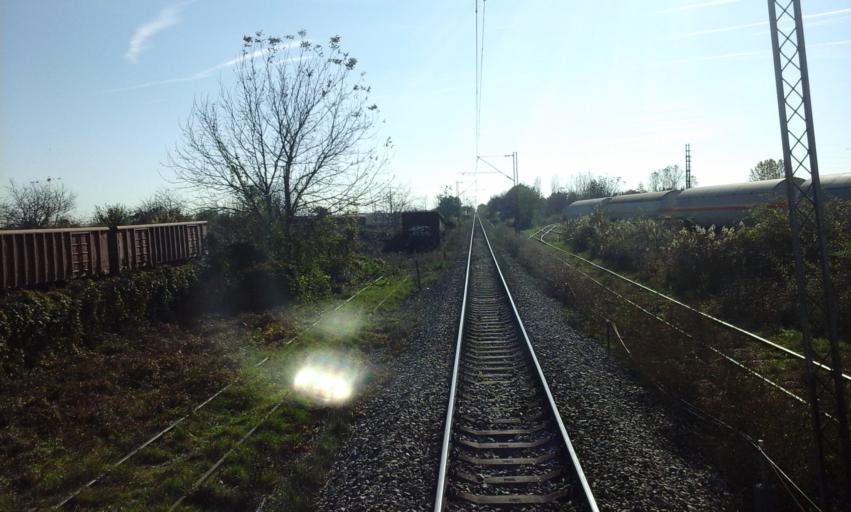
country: RS
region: Autonomna Pokrajina Vojvodina
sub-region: Severnobacki Okrug
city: Subotica
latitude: 46.0601
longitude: 19.6869
